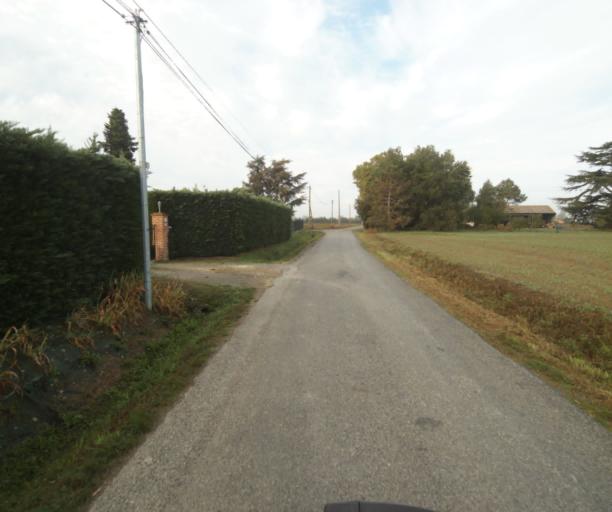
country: FR
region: Midi-Pyrenees
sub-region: Departement du Tarn-et-Garonne
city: Montech
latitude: 43.9486
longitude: 1.2316
